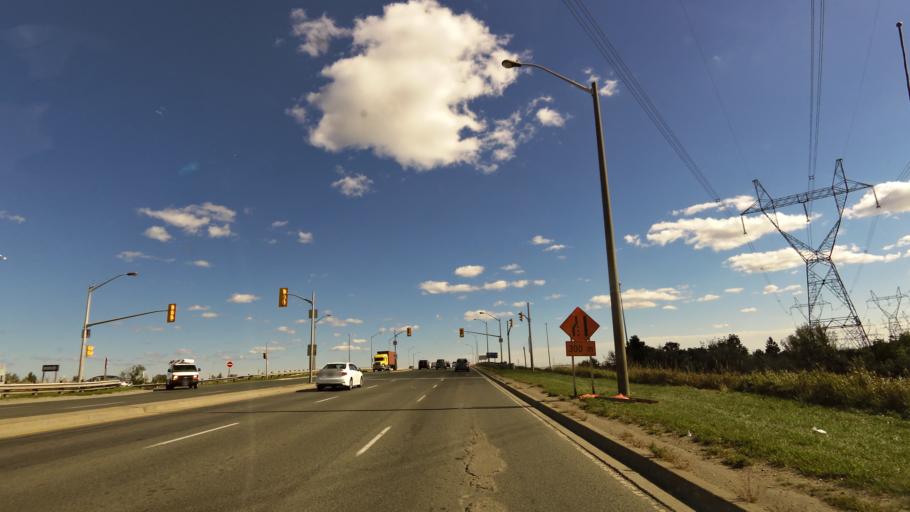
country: CA
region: Ontario
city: Brampton
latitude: 43.7370
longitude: -79.6633
